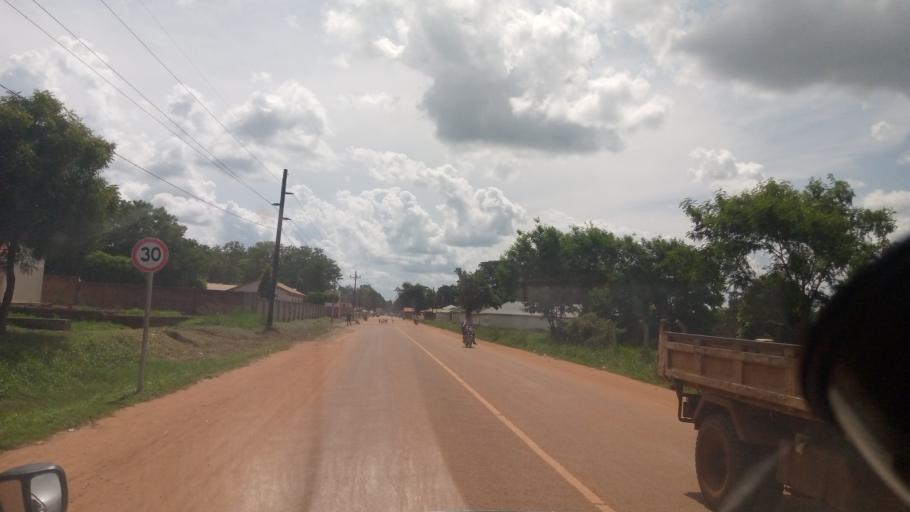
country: UG
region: Northern Region
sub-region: Lira District
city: Lira
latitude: 2.2488
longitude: 32.9045
